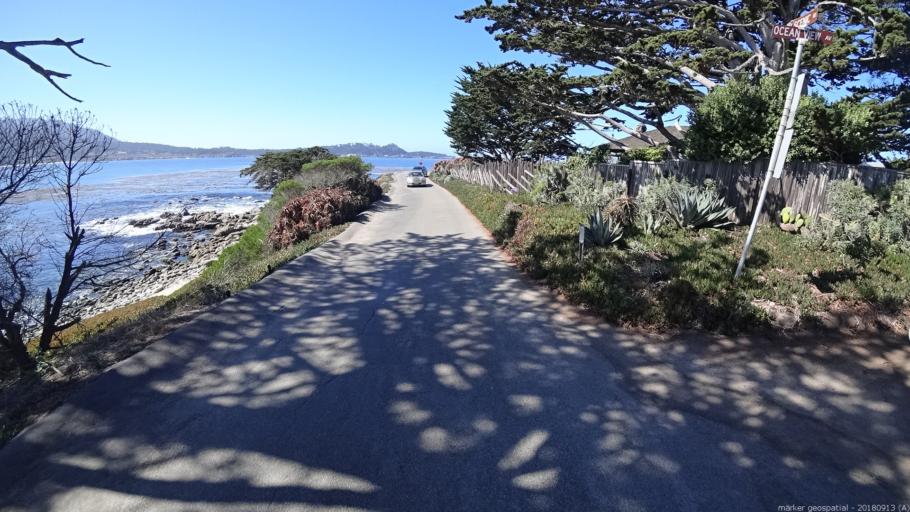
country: US
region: California
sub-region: Monterey County
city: Carmel-by-the-Sea
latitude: 36.5400
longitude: -121.9315
